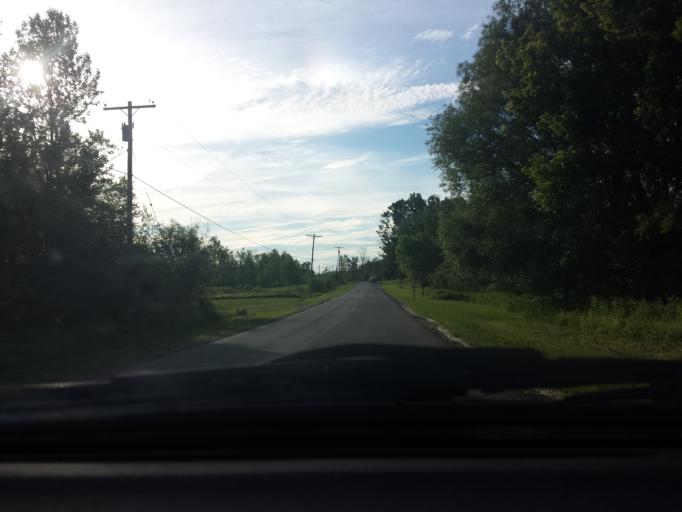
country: US
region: New York
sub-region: St. Lawrence County
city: Norwood
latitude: 44.7221
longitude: -74.9491
